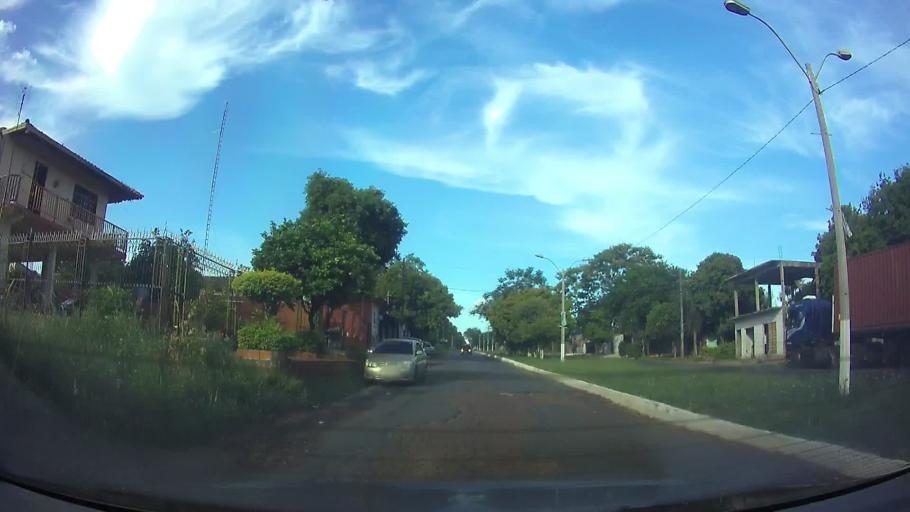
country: PY
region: Central
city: San Antonio
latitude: -25.4313
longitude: -57.5499
